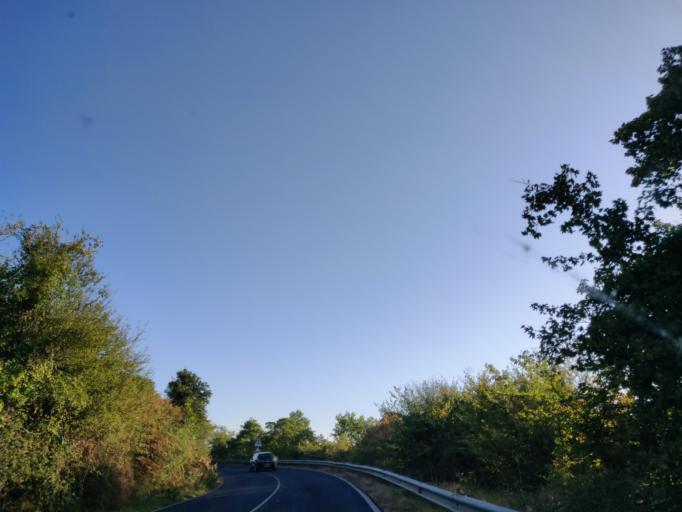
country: IT
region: Latium
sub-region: Provincia di Viterbo
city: Gradoli
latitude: 42.6435
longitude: 11.8389
